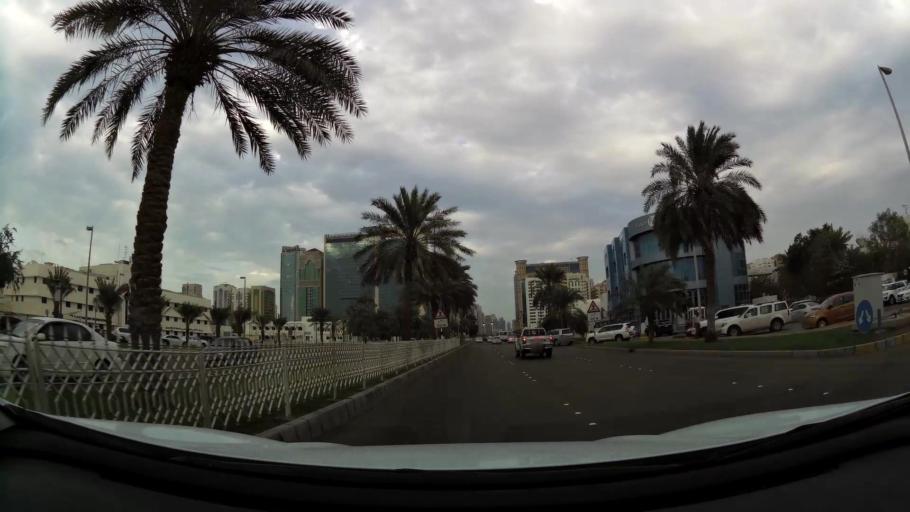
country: AE
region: Abu Dhabi
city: Abu Dhabi
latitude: 24.4670
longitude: 54.3671
